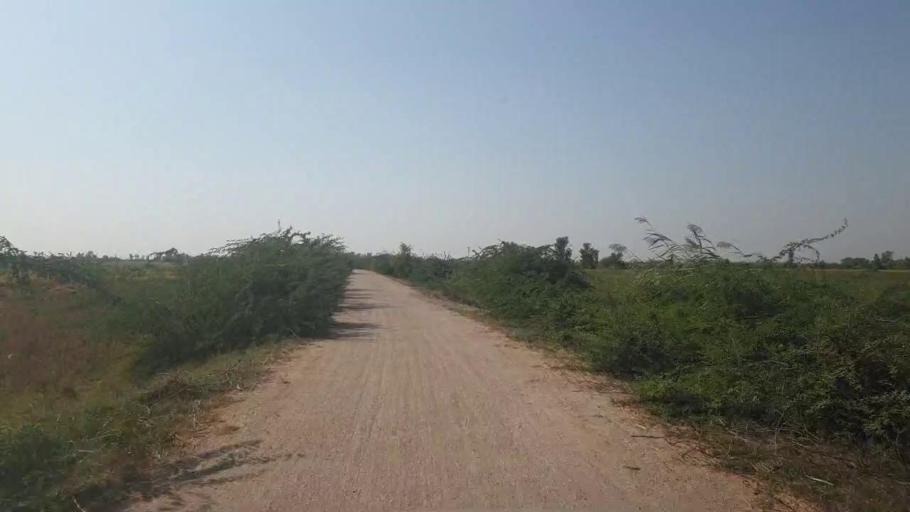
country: PK
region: Sindh
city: Badin
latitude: 24.5574
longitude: 68.8440
